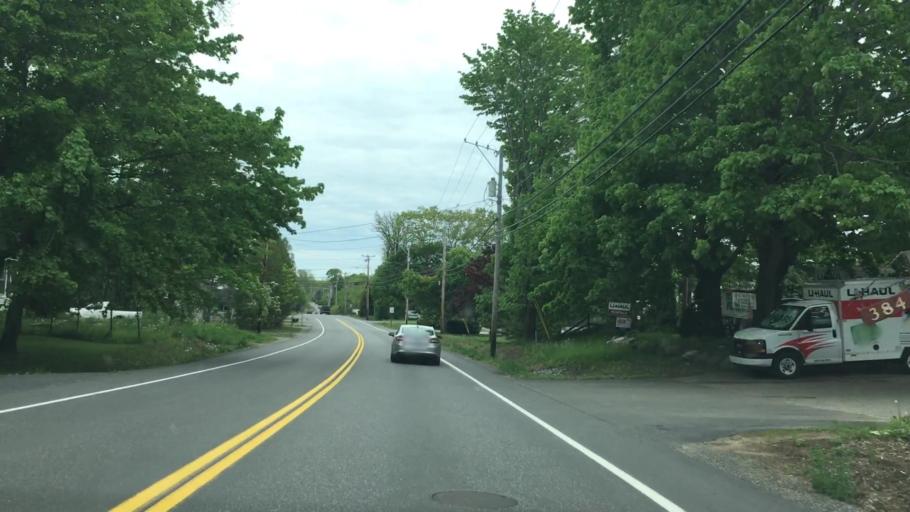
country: US
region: Maine
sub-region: Knox County
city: Rockland
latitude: 44.1181
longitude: -69.1267
